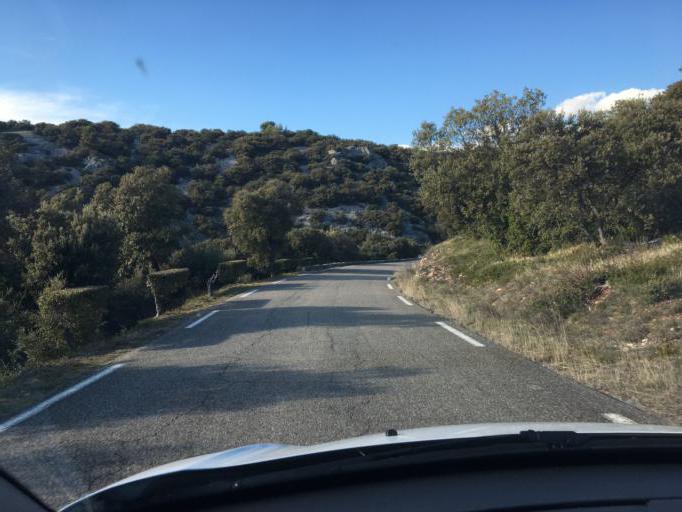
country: FR
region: Provence-Alpes-Cote d'Azur
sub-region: Departement du Vaucluse
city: Villes-sur-Auzon
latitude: 44.0557
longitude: 5.2471
